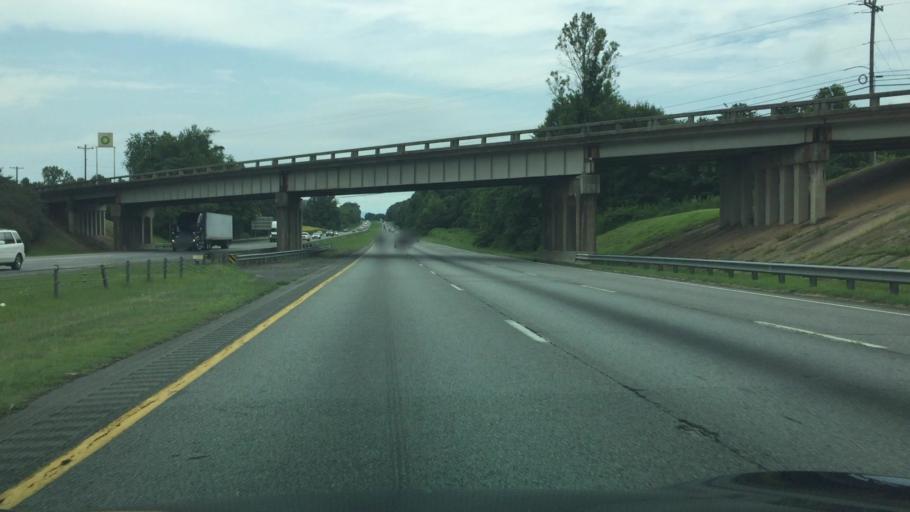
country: US
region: North Carolina
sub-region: Yadkin County
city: Jonesville
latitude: 36.1971
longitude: -80.8114
